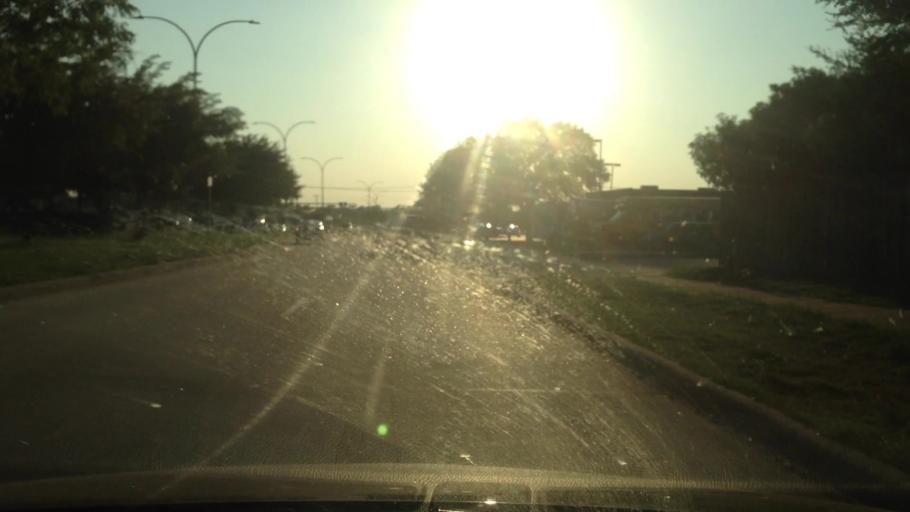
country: US
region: Texas
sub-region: Tarrant County
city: Dalworthington Gardens
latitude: 32.6492
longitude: -97.1325
